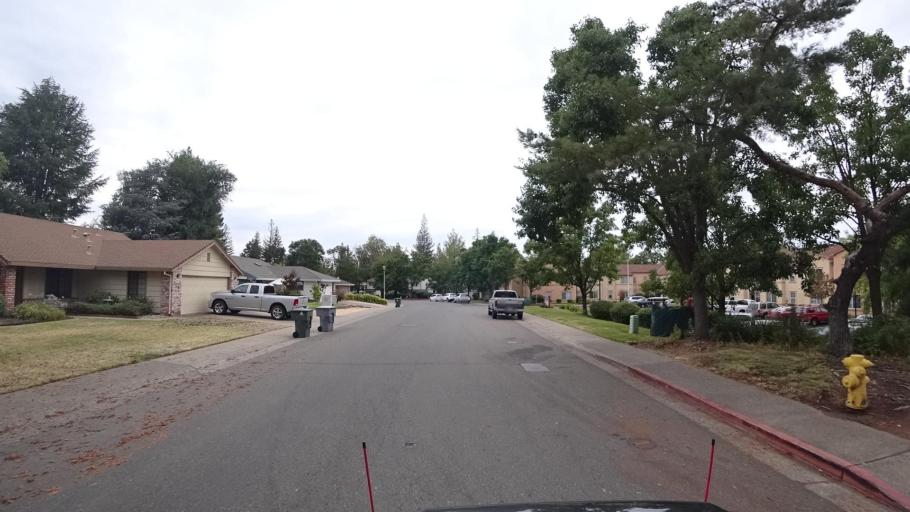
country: US
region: California
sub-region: Placer County
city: Rocklin
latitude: 38.7840
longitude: -121.2501
